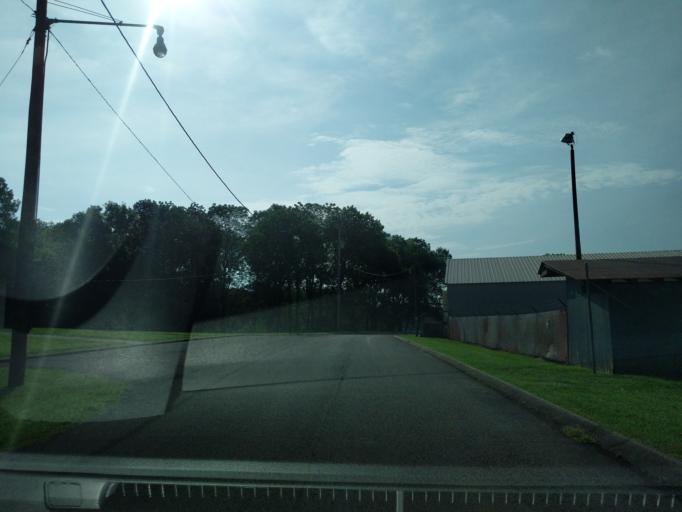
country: US
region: Tennessee
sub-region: Sumner County
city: Hendersonville
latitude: 36.2982
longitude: -86.6531
